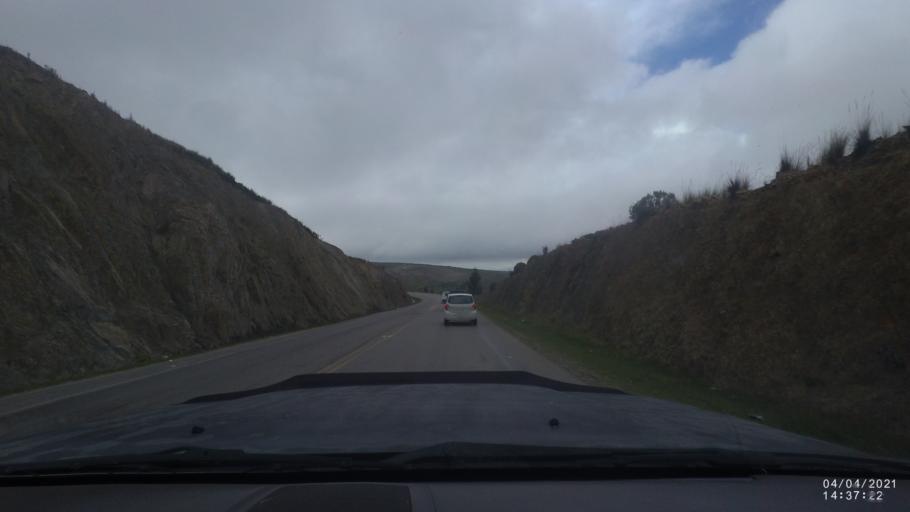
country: BO
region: Cochabamba
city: Irpa Irpa
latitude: -17.6687
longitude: -66.4833
